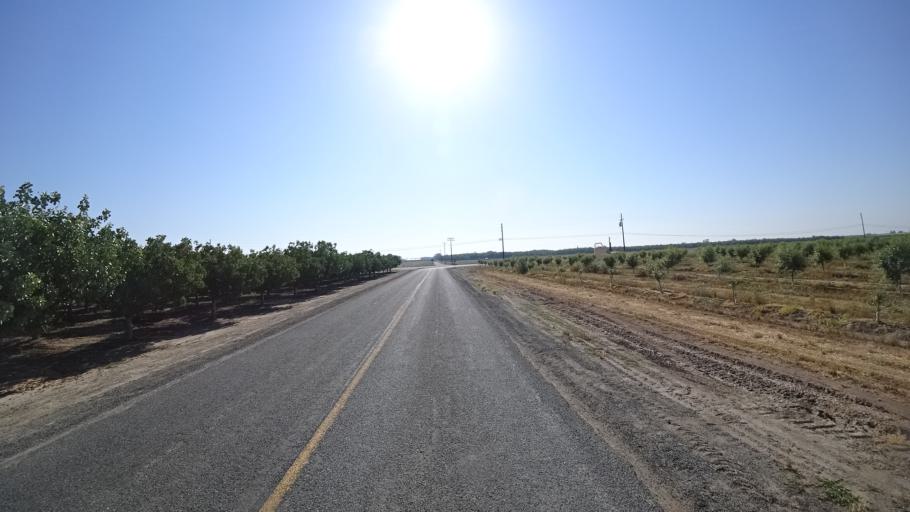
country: US
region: California
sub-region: Kings County
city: Lucerne
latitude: 36.3935
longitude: -119.6746
